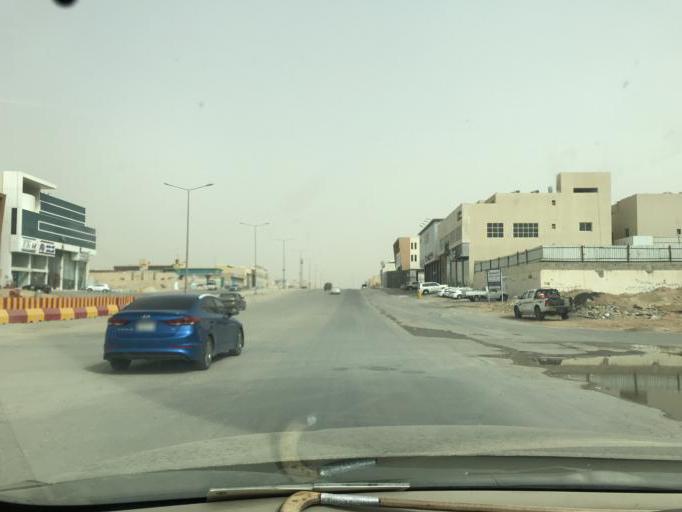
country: SA
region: Ar Riyad
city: Riyadh
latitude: 24.8157
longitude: 46.5980
